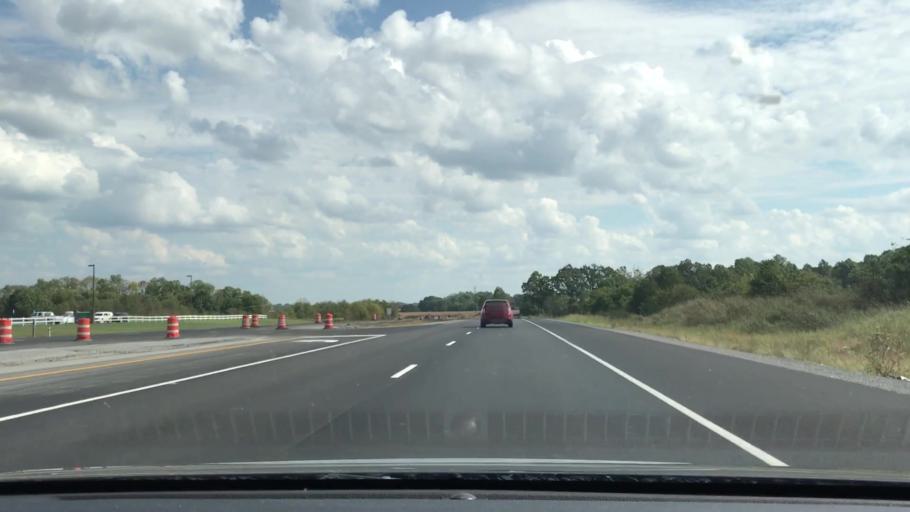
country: US
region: Kentucky
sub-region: Trigg County
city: Cadiz
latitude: 36.8604
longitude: -87.8051
